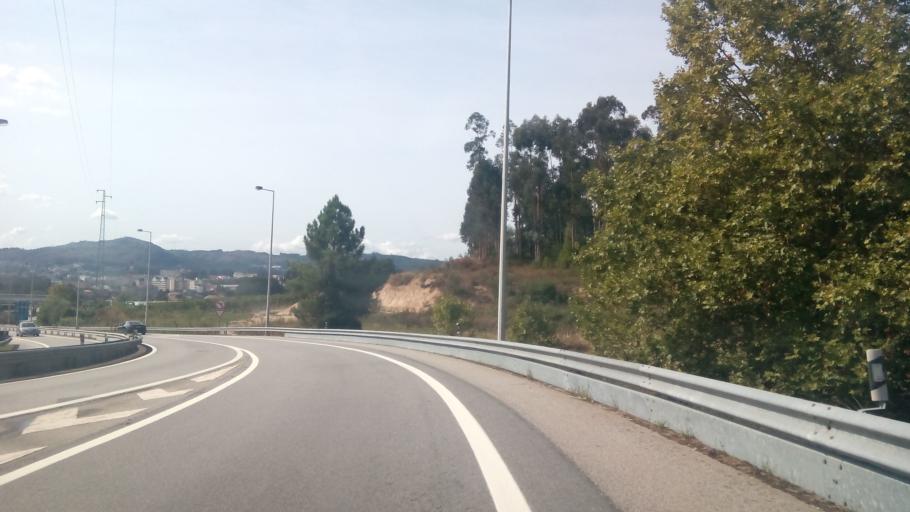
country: PT
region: Porto
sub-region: Paredes
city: Paredes
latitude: 41.2029
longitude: -8.3092
